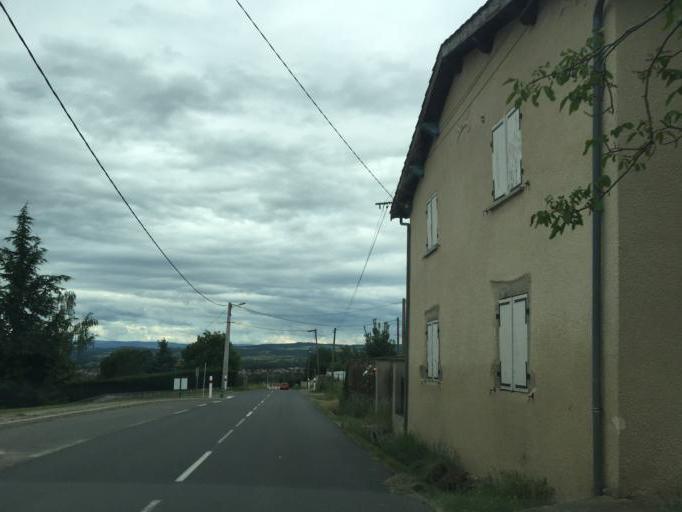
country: FR
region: Rhone-Alpes
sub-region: Departement de la Loire
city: Saint-Marcellin-en-Forez
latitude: 45.5056
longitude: 4.1378
